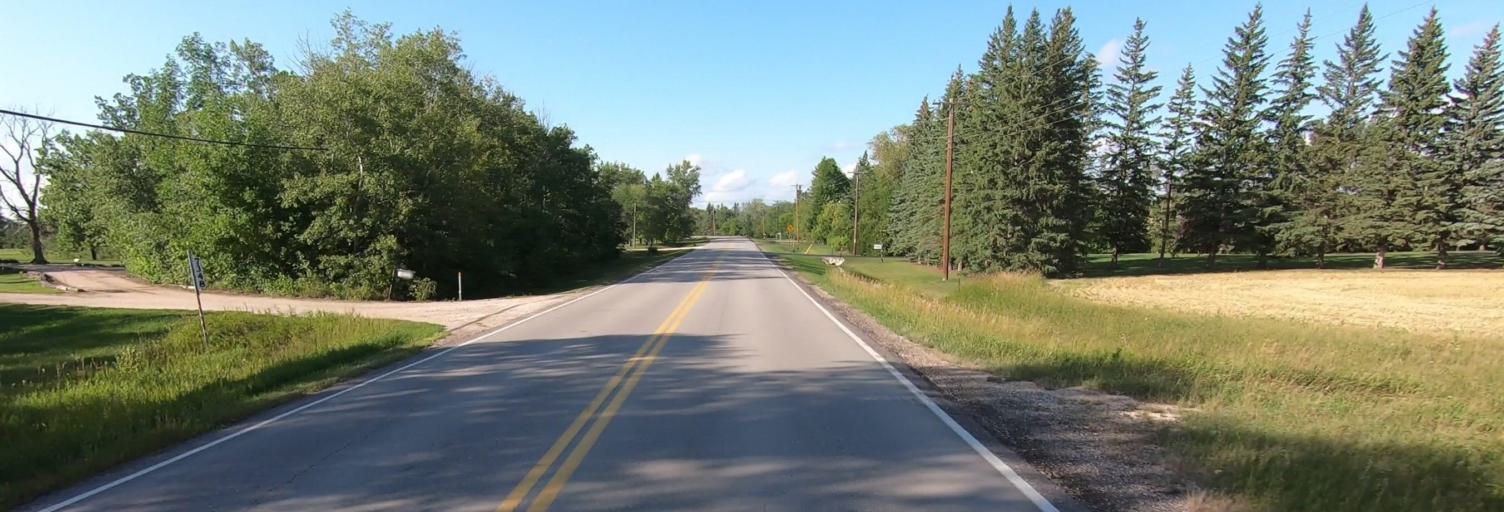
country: CA
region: Manitoba
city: Selkirk
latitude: 50.0984
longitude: -96.9329
